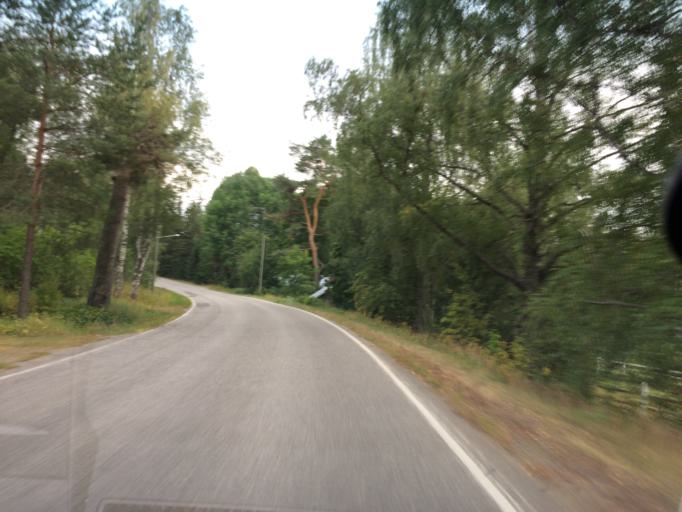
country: FI
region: Pirkanmaa
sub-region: Tampere
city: Luopioinen
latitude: 61.2539
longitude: 24.7065
